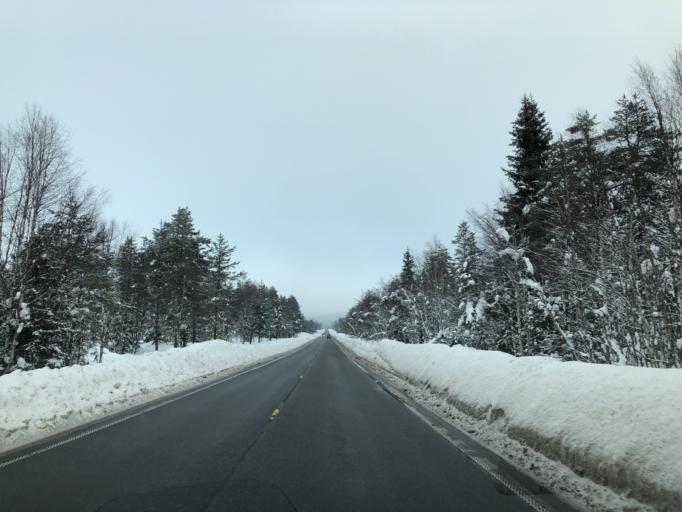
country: NO
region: Hedmark
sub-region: Elverum
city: Elverum
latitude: 61.0290
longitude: 11.8640
